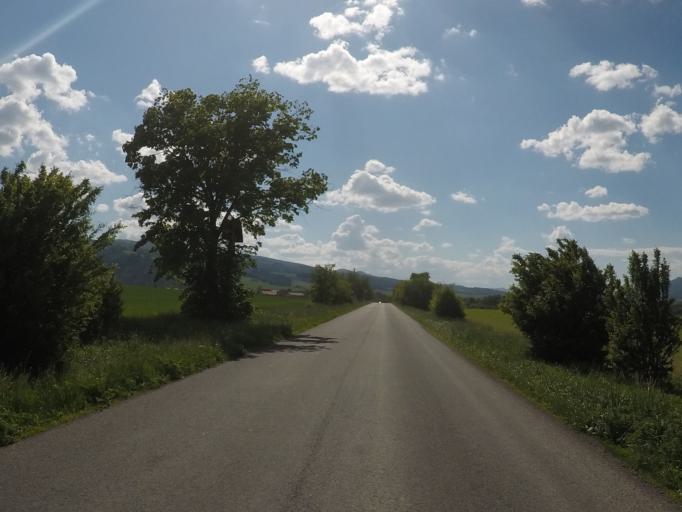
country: SK
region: Presovsky
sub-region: Okres Poprad
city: Poprad
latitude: 48.9907
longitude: 20.3219
